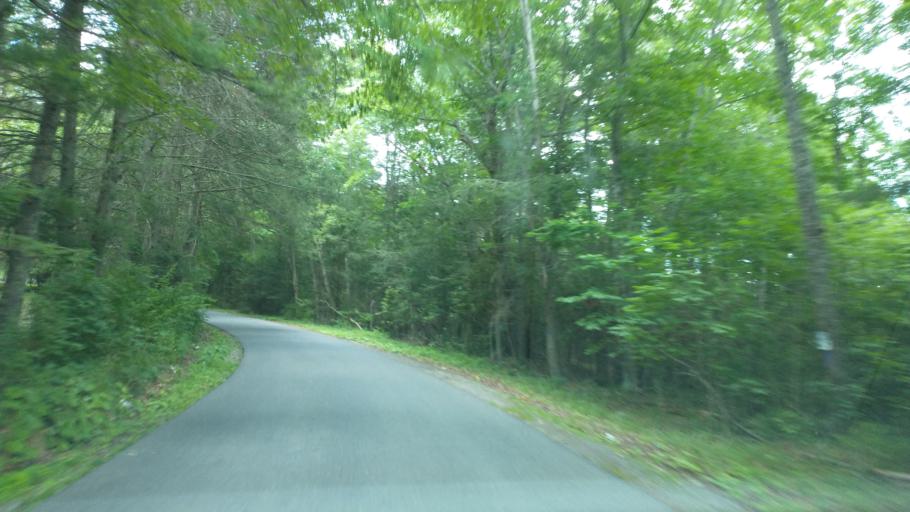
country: US
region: West Virginia
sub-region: Mercer County
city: Athens
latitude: 37.4586
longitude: -81.0469
